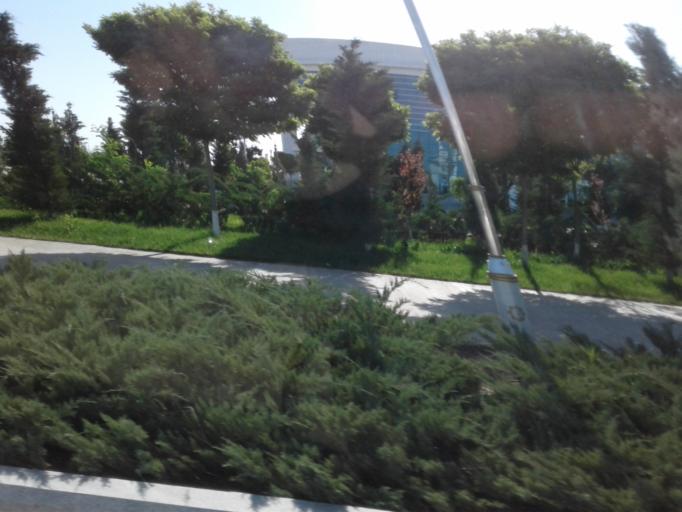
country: TM
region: Balkan
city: Turkmenbasy
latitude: 39.9782
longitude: 52.8281
